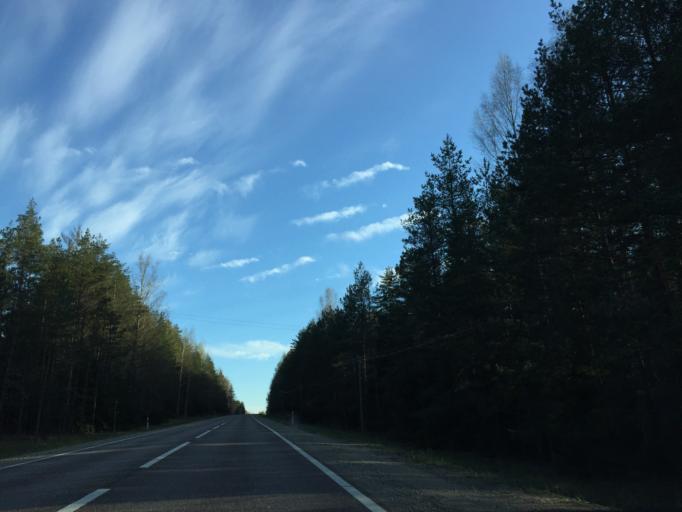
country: LV
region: Valkas Rajons
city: Valka
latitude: 57.7347
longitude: 25.9431
